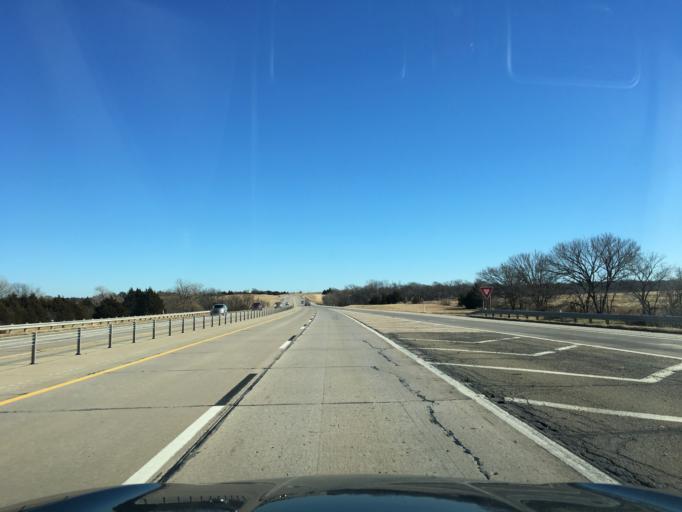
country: US
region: Oklahoma
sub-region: Payne County
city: Stillwater
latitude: 36.2402
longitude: -96.9446
